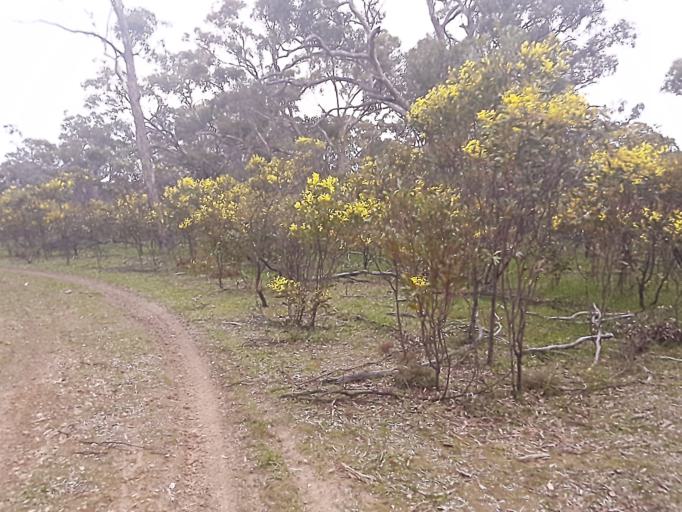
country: AU
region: Victoria
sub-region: Ararat
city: Ararat
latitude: -37.2166
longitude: 142.9622
